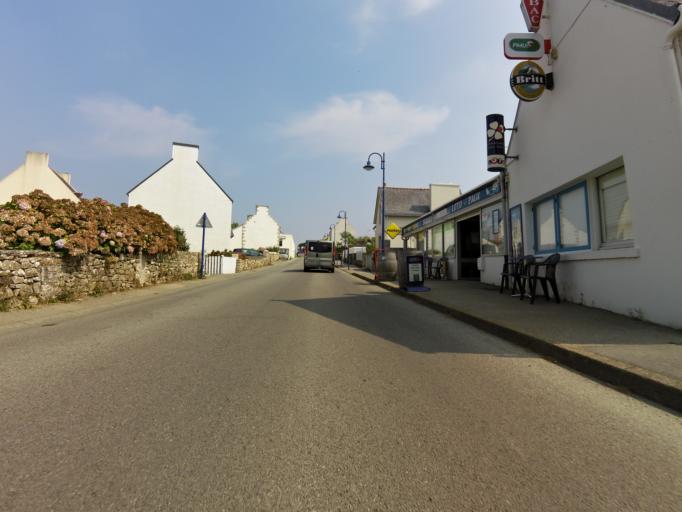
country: FR
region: Brittany
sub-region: Departement du Finistere
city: Plogoff
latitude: 48.0365
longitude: -4.6665
